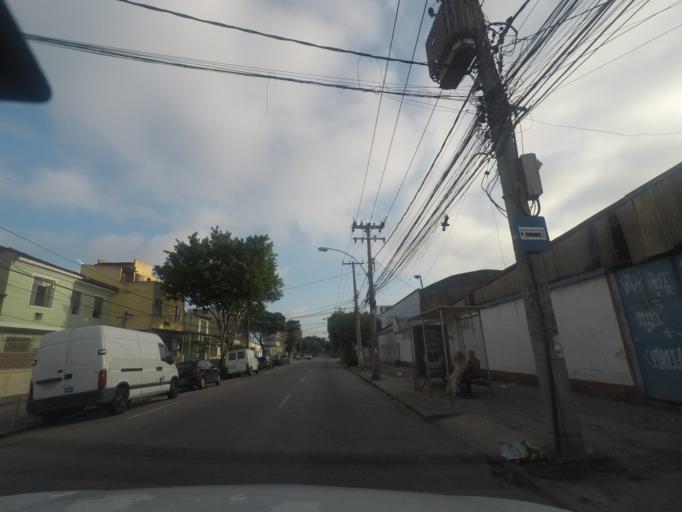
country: BR
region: Rio de Janeiro
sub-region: Duque De Caxias
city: Duque de Caxias
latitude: -22.8358
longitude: -43.2784
